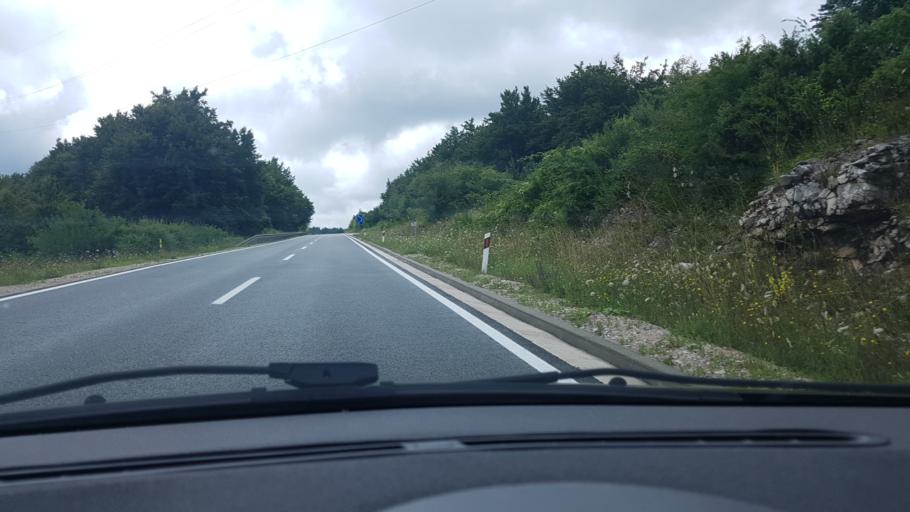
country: HR
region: Licko-Senjska
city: Jezerce
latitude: 44.8582
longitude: 15.6936
